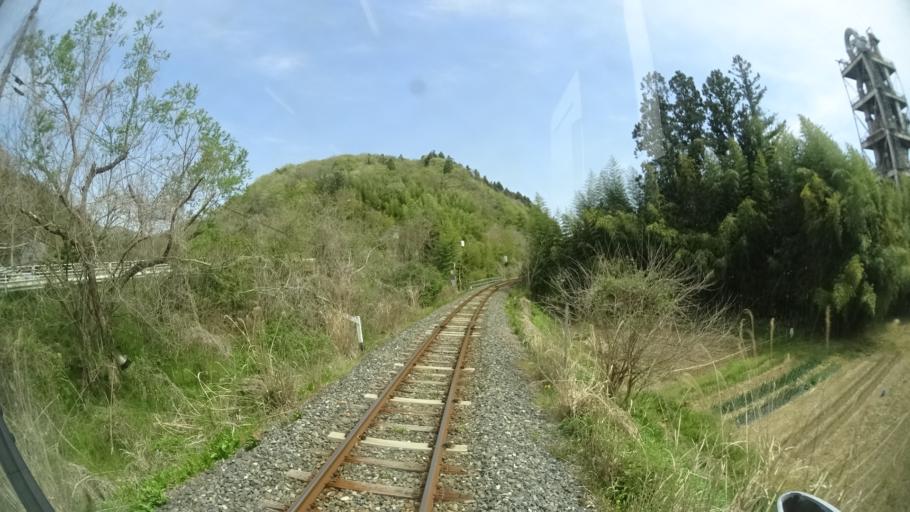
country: JP
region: Iwate
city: Ichinoseki
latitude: 38.9835
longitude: 141.2426
